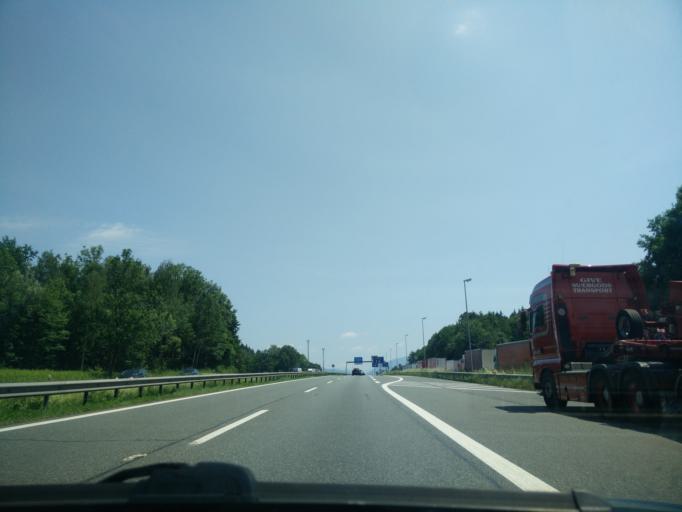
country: DE
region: Bavaria
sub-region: Upper Bavaria
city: Piding
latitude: 47.7681
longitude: 12.9342
